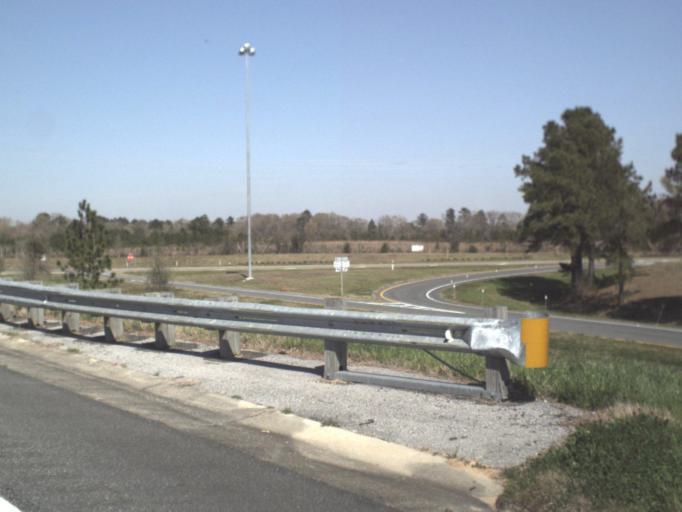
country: US
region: Florida
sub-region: Jackson County
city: Marianna
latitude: 30.7524
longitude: -85.2706
